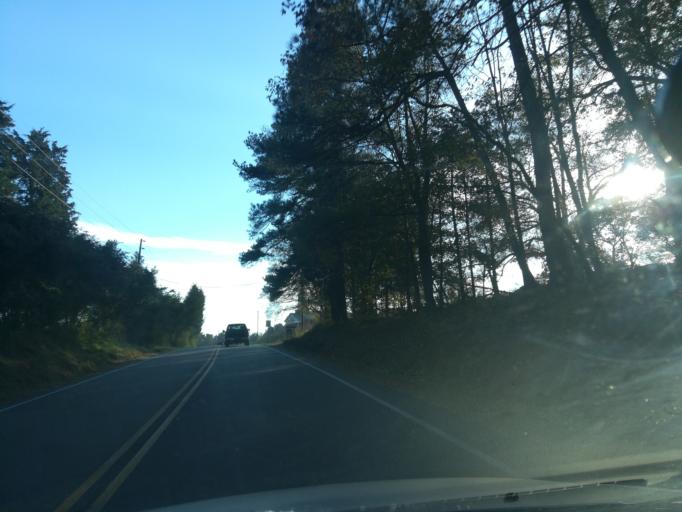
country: US
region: North Carolina
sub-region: Orange County
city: Chapel Hill
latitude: 35.9734
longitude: -79.0077
